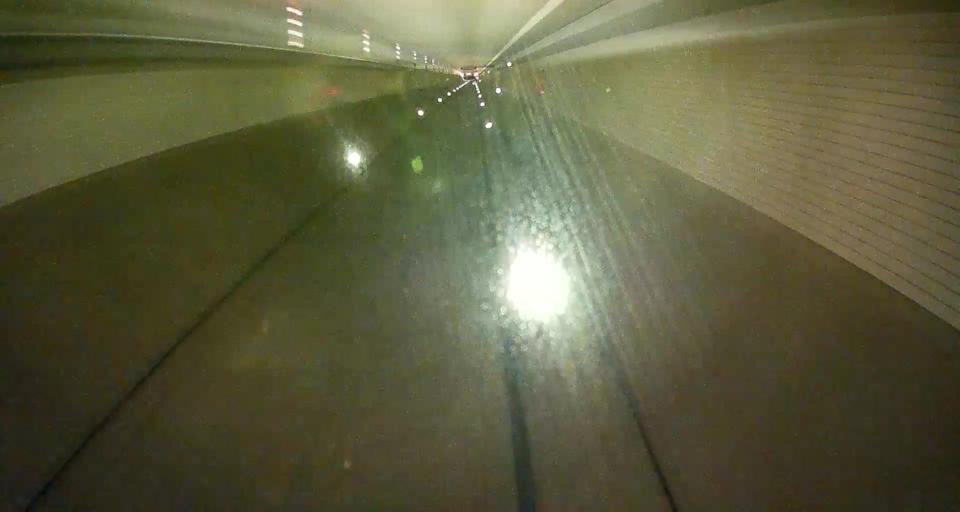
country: JP
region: Iwate
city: Miyako
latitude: 39.9307
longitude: 141.8607
